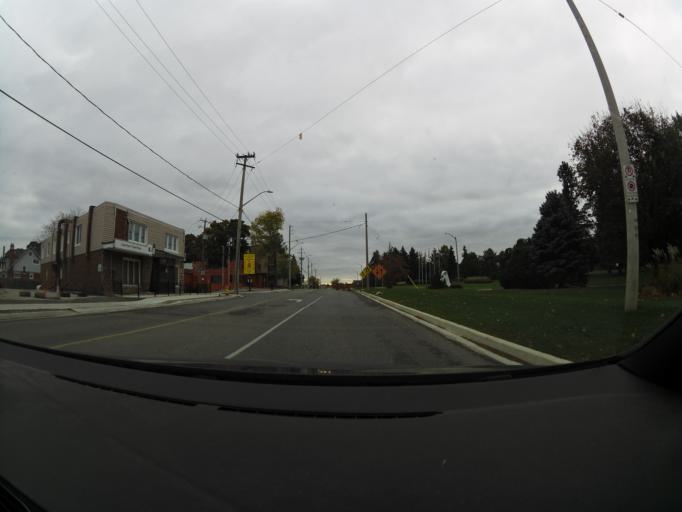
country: CA
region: Ontario
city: Kitchener
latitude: 43.4393
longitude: -80.4654
